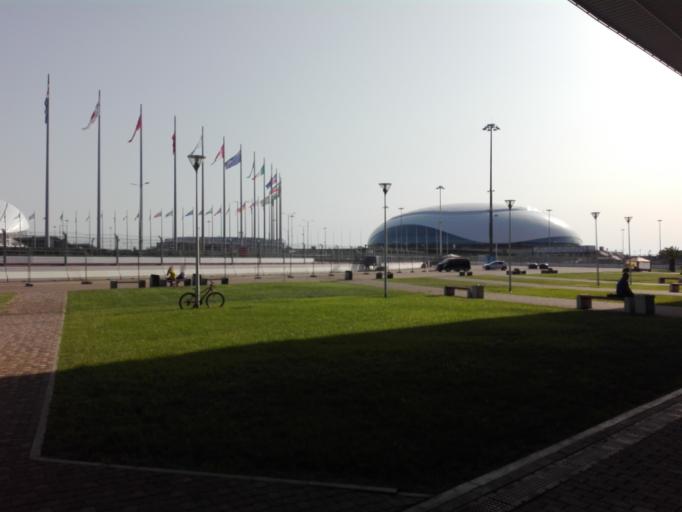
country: RU
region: Krasnodarskiy
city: Adler
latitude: 43.4079
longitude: 39.9539
